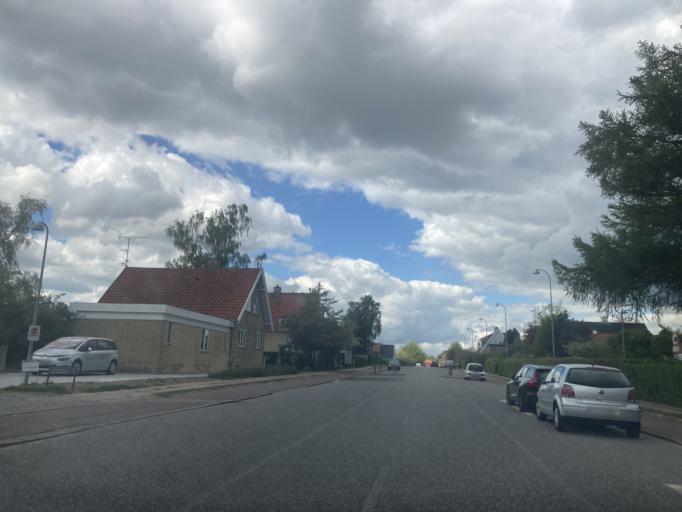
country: DK
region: Capital Region
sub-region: Gladsaxe Municipality
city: Buddinge
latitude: 55.7607
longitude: 12.4844
